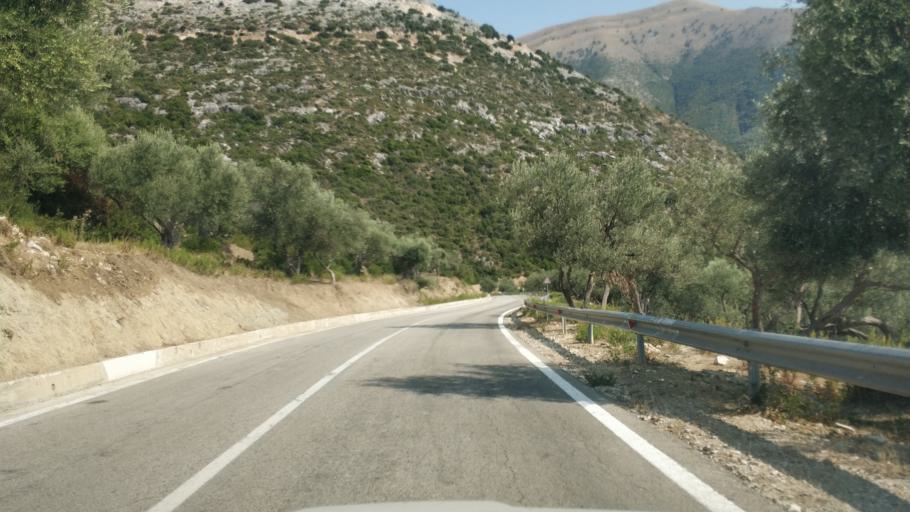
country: AL
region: Vlore
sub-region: Rrethi i Sarandes
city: Lukove
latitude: 40.0111
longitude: 19.9000
